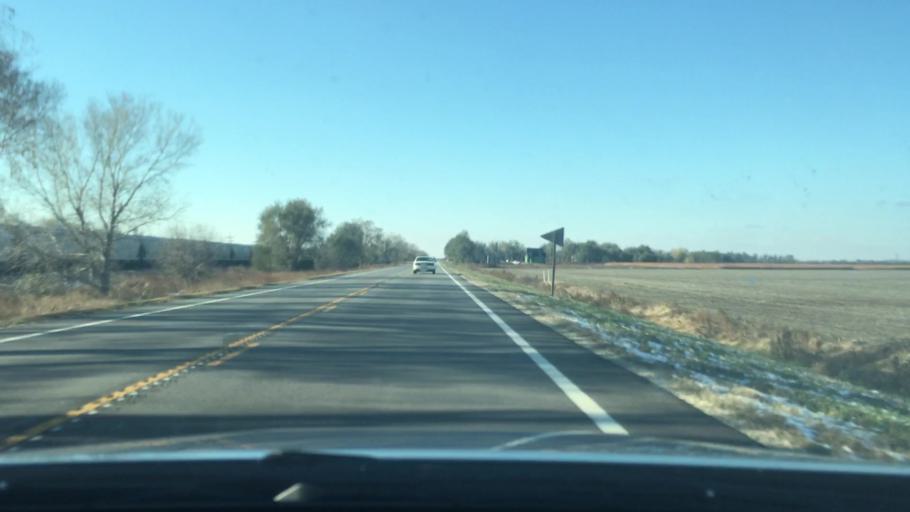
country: US
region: Kansas
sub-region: Reno County
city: Nickerson
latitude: 38.1080
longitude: -98.0260
